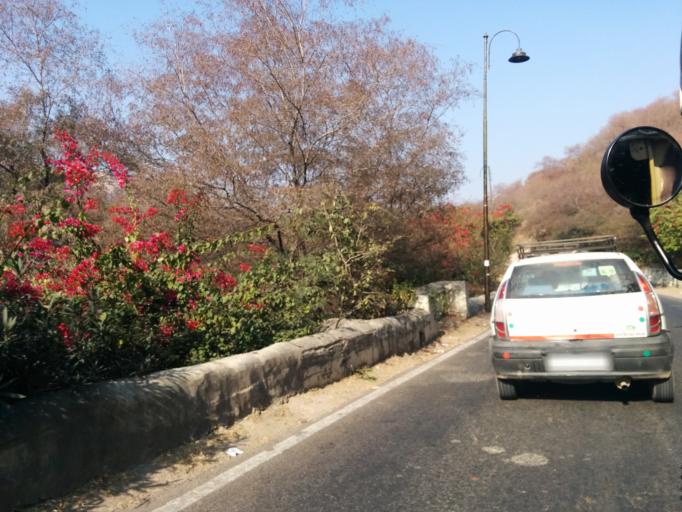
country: IN
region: Rajasthan
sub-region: Jaipur
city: Jaipur
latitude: 26.9735
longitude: 75.8518
